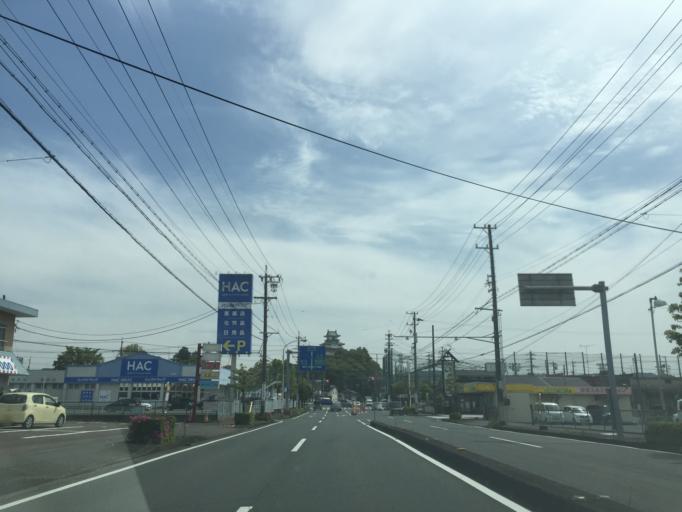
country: JP
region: Shizuoka
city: Kakegawa
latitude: 34.7787
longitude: 138.0136
